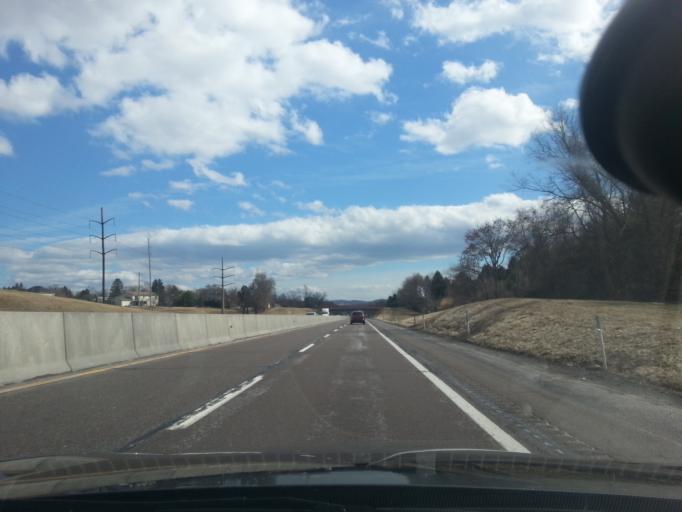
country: US
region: Pennsylvania
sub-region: Lehigh County
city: Wescosville
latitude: 40.5574
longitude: -75.5440
